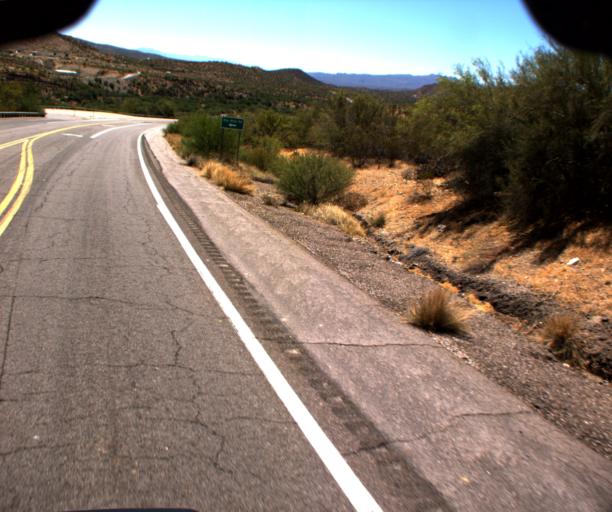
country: US
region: Arizona
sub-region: Pinal County
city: Kearny
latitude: 33.1298
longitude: -110.9813
